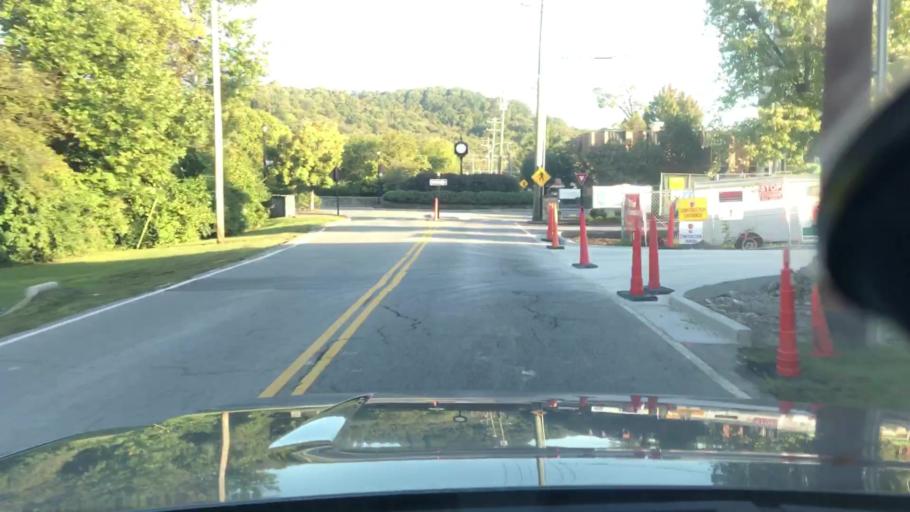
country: US
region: Tennessee
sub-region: Williamson County
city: Brentwood
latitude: 36.0342
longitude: -86.7855
